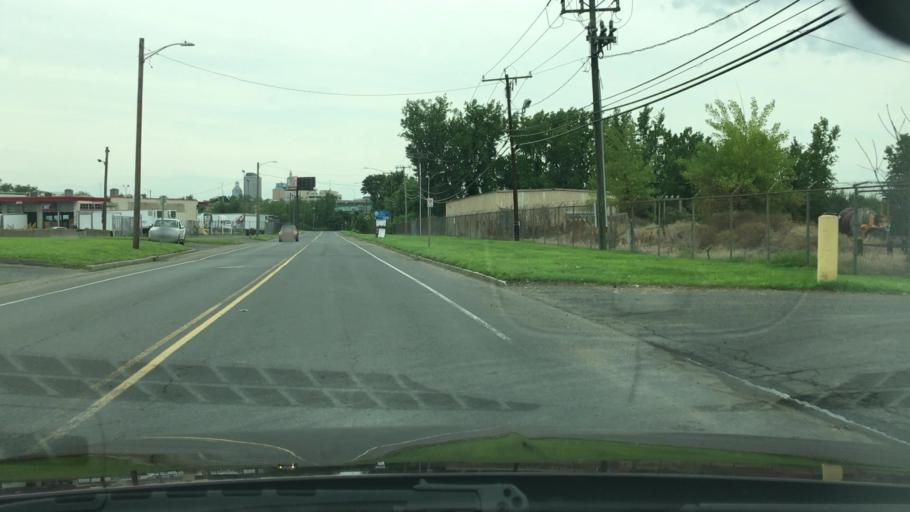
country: US
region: Connecticut
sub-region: Hartford County
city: Wethersfield
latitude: 41.7461
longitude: -72.6548
